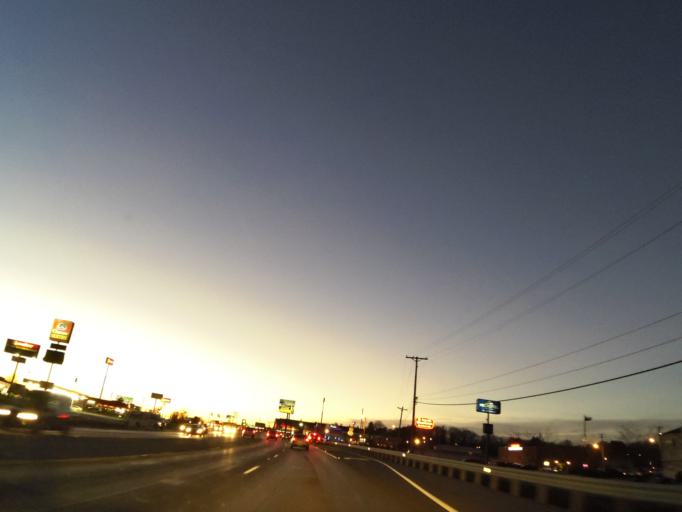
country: US
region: Kentucky
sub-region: Laurel County
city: London
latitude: 37.1115
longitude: -84.0949
